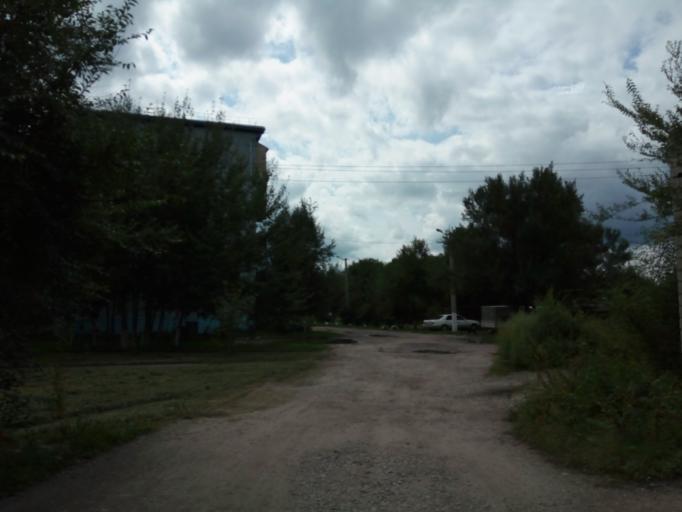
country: RU
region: Primorskiy
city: Dal'nerechensk
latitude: 45.9420
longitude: 133.8147
